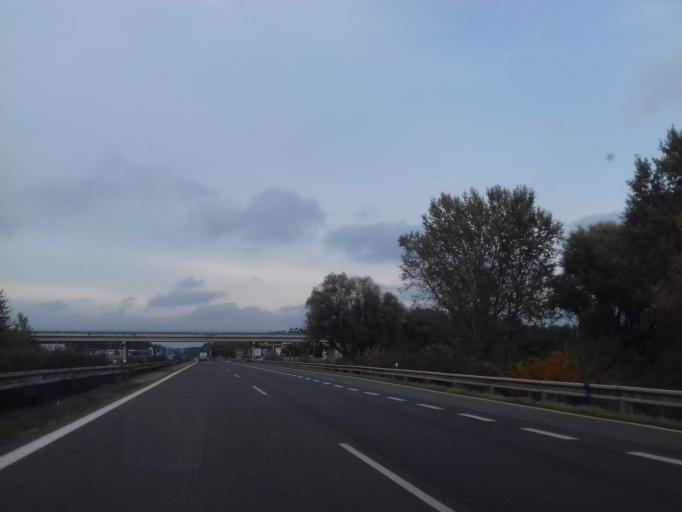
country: AT
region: Lower Austria
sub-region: Politischer Bezirk Mistelbach
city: Rabensburg
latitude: 48.6108
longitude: 17.0140
